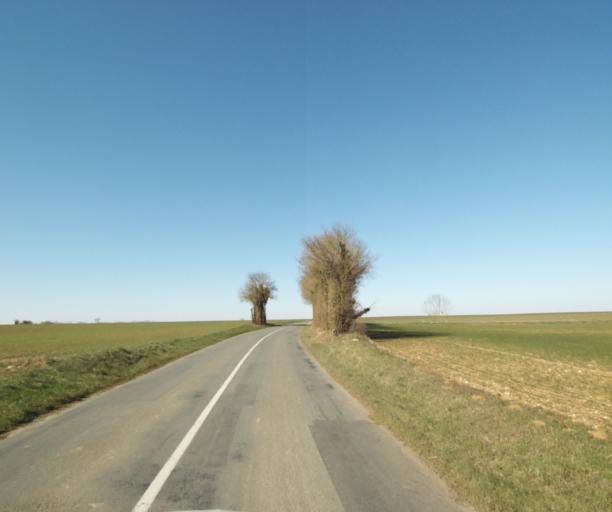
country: FR
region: Poitou-Charentes
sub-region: Departement des Deux-Sevres
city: Saint-Maxire
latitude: 46.3654
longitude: -0.4902
